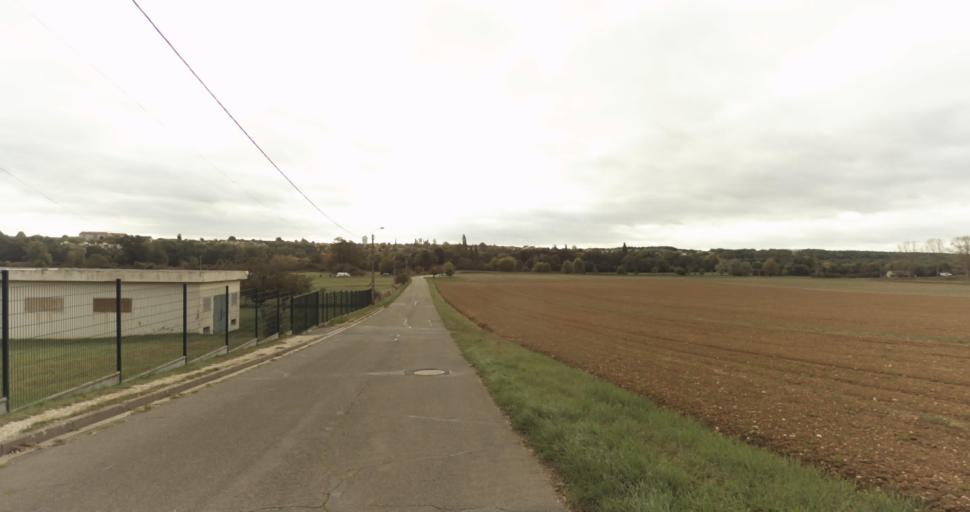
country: FR
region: Centre
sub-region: Departement d'Eure-et-Loir
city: Vernouillet
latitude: 48.7226
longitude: 1.3497
